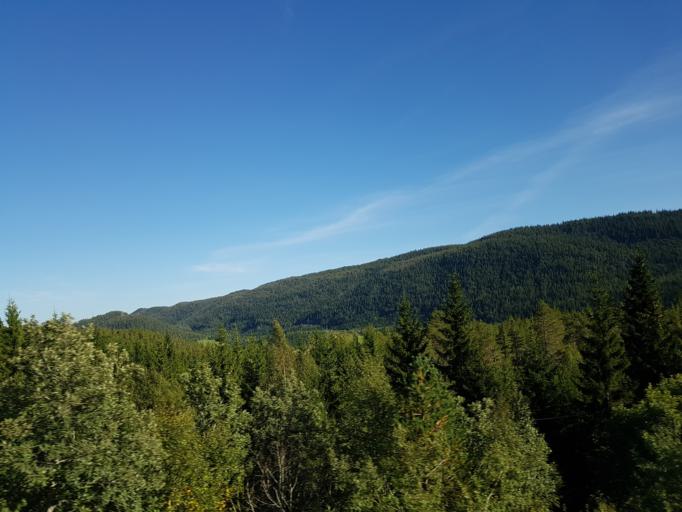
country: NO
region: Sor-Trondelag
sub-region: Afjord
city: A i Afjord
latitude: 63.6904
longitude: 10.2448
